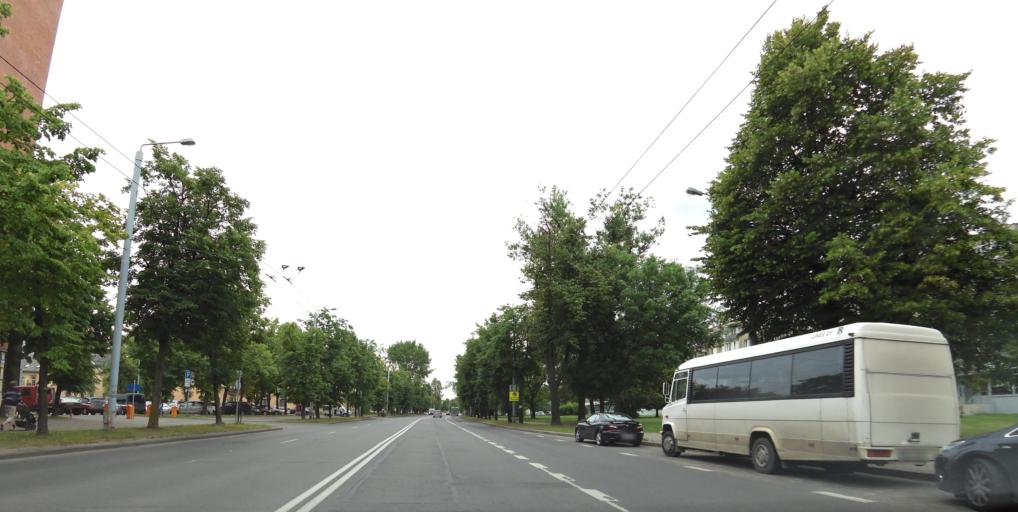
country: LT
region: Vilnius County
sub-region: Vilnius
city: Vilnius
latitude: 54.7111
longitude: 25.2863
